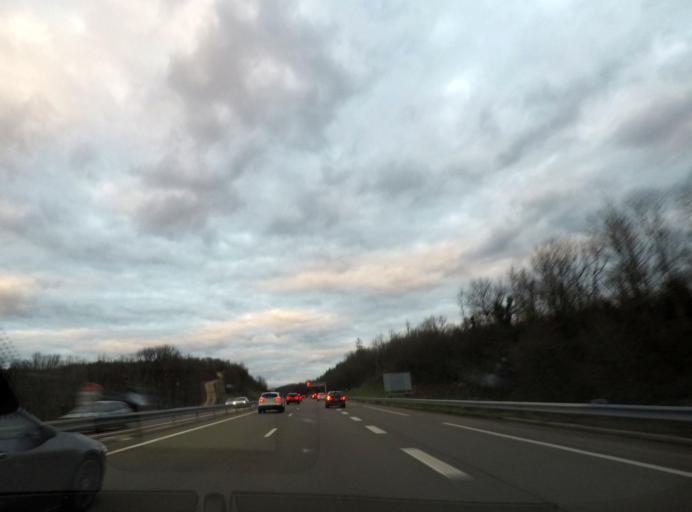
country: FR
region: Rhone-Alpes
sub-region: Departement de l'Ain
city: Saint-Martin-du-Frene
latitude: 46.1205
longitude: 5.4944
